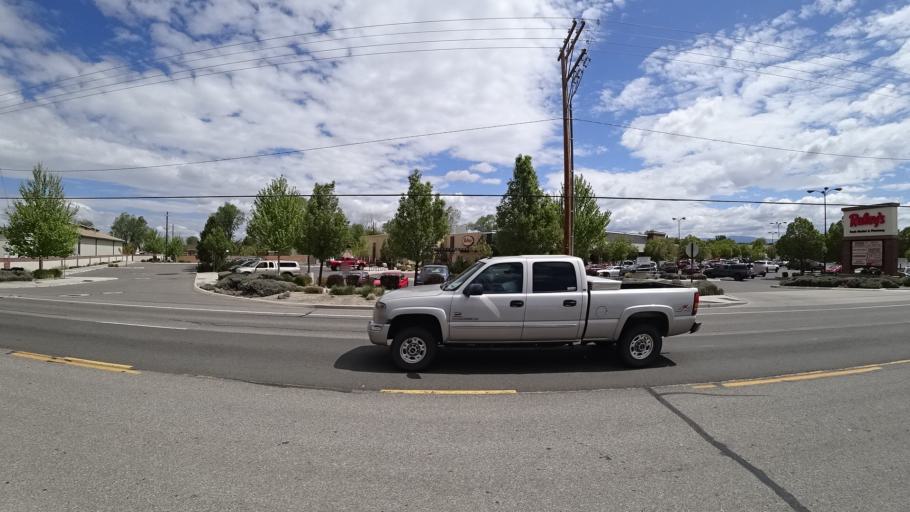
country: US
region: Nevada
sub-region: Douglas County
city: Gardnerville
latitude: 38.9377
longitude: -119.7422
